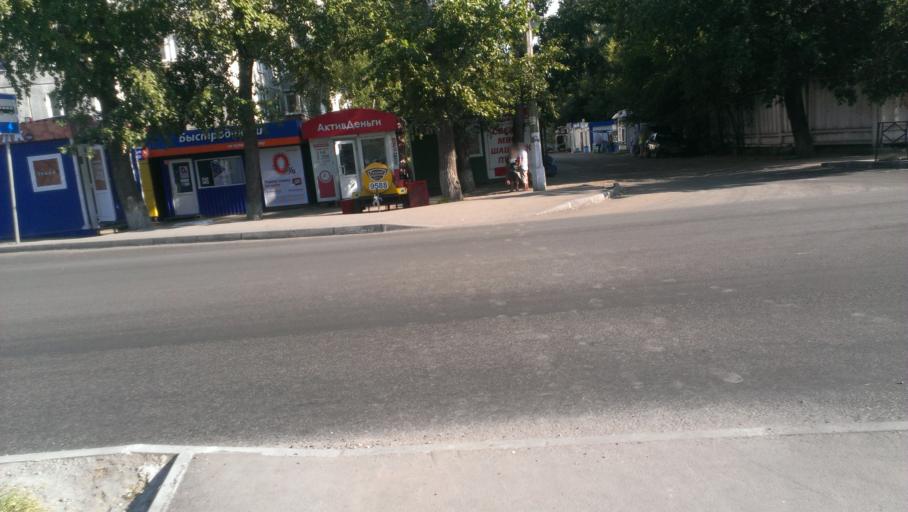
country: RU
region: Altai Krai
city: Novosilikatnyy
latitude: 53.3077
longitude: 83.6207
